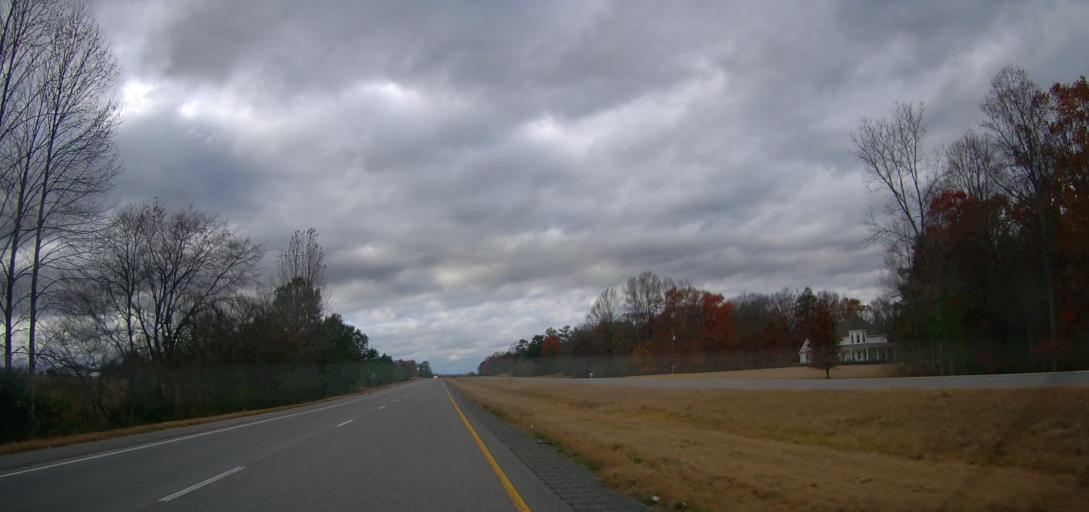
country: US
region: Alabama
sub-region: Lawrence County
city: Town Creek
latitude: 34.5957
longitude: -87.4356
